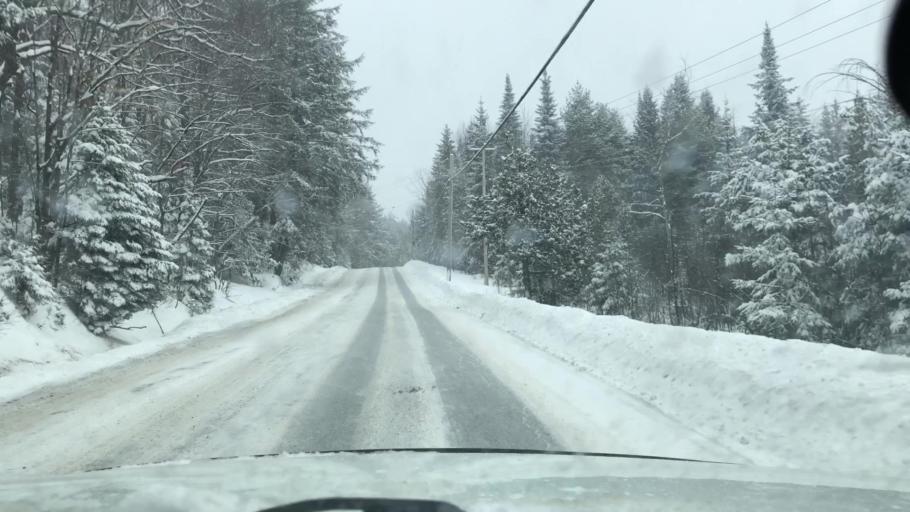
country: CA
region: Quebec
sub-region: Outaouais
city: Gatineau
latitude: 45.5162
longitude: -75.8431
